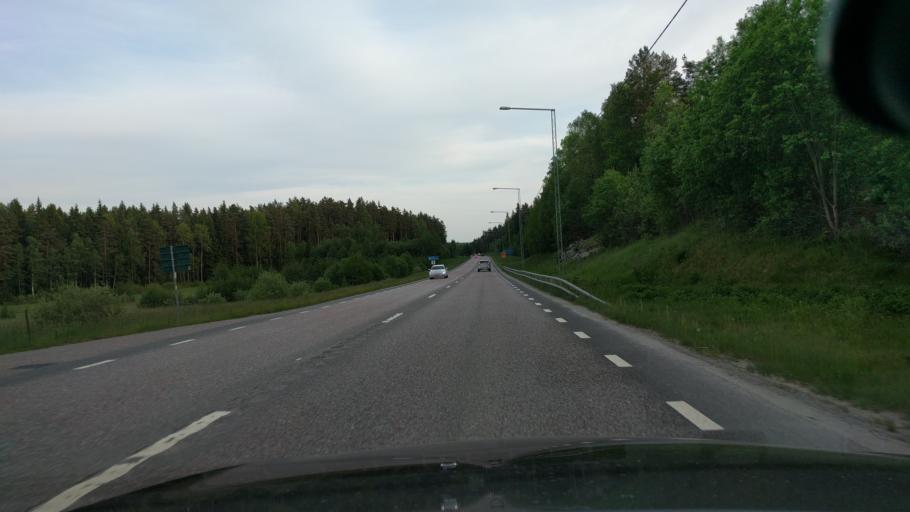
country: SE
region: Stockholm
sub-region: Vallentuna Kommun
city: Vallentuna
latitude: 59.5049
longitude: 18.0992
